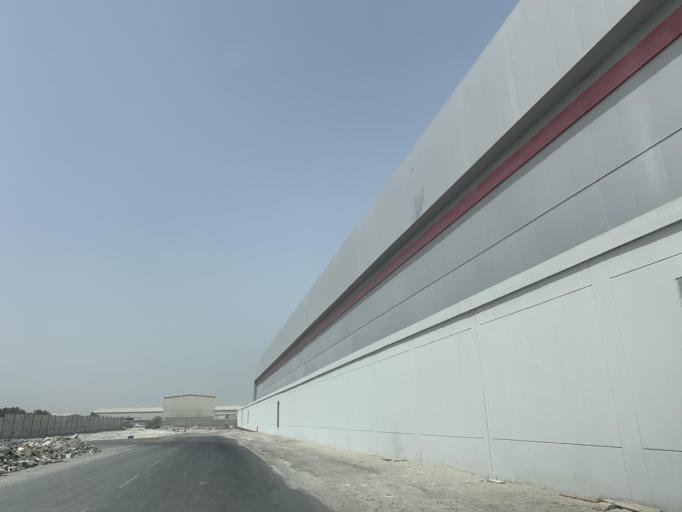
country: BH
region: Northern
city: Madinat `Isa
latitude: 26.1892
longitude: 50.5302
